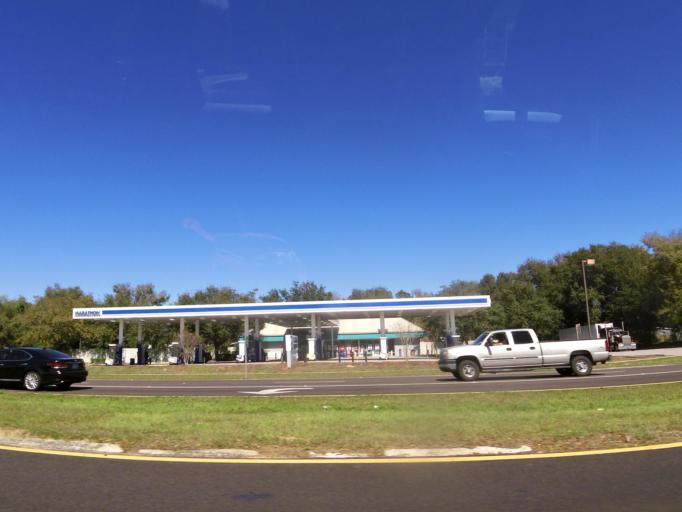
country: US
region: Florida
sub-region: Orange County
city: Apopka
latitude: 28.6853
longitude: -81.5337
